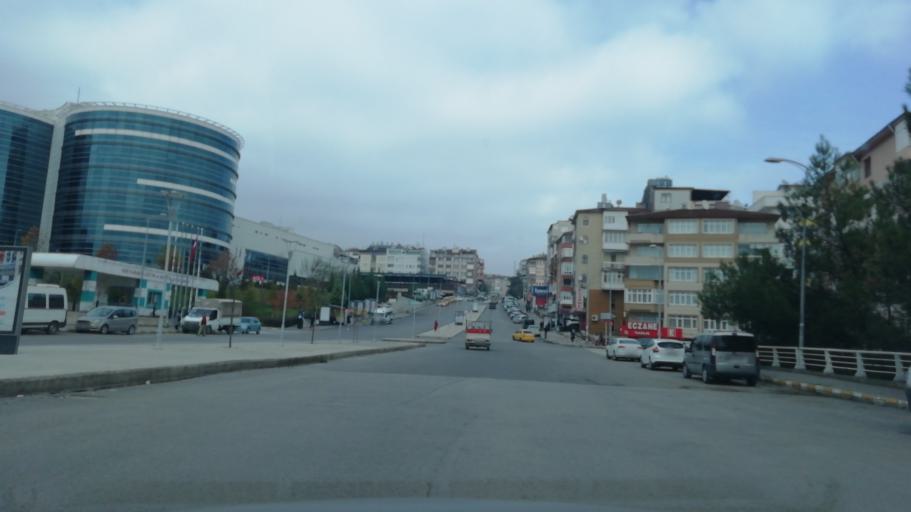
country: TR
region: Karabuk
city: Karabuk
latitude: 41.2072
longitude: 32.6194
